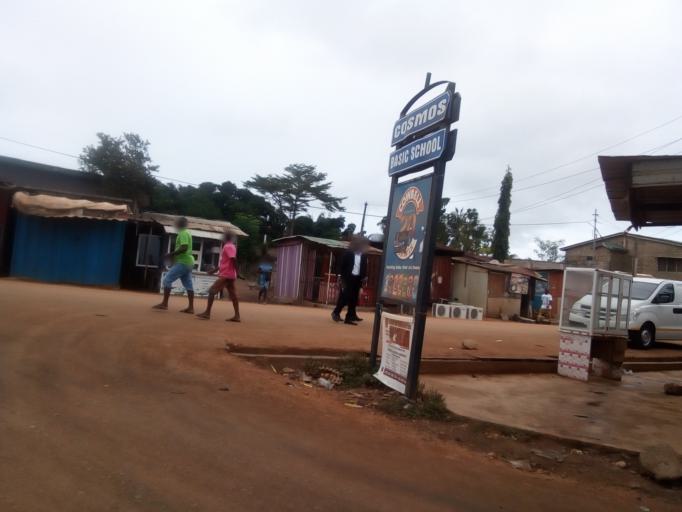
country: GH
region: Greater Accra
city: Dome
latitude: 5.6097
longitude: -0.2564
